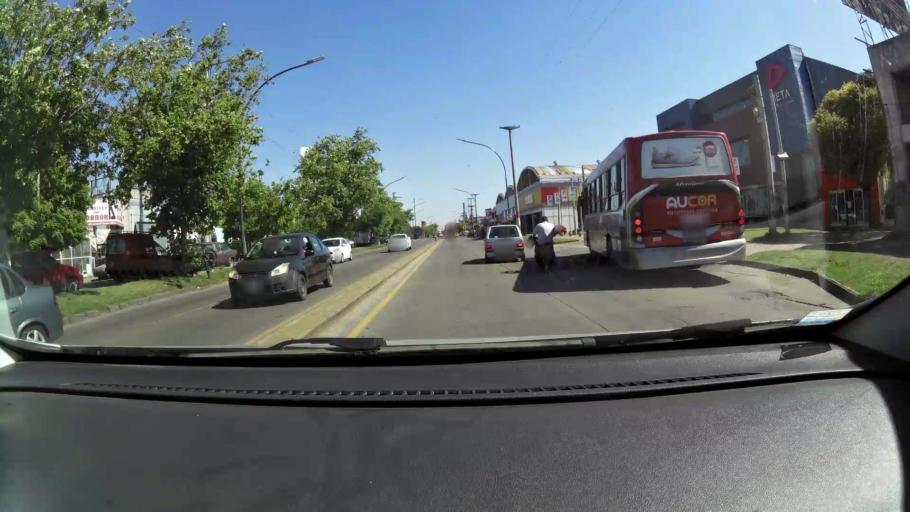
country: AR
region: Cordoba
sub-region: Departamento de Capital
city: Cordoba
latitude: -31.3789
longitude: -64.1760
